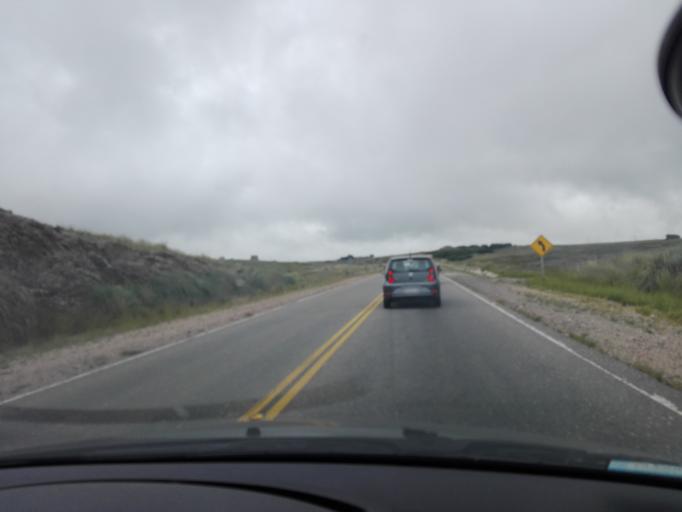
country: AR
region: Cordoba
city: Cuesta Blanca
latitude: -31.6097
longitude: -64.7515
